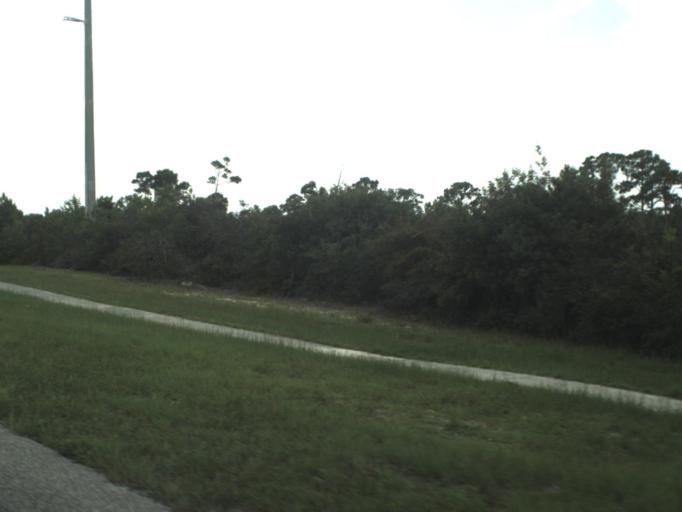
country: US
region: Florida
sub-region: Martin County
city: Hobe Sound
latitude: 27.0960
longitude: -80.1572
